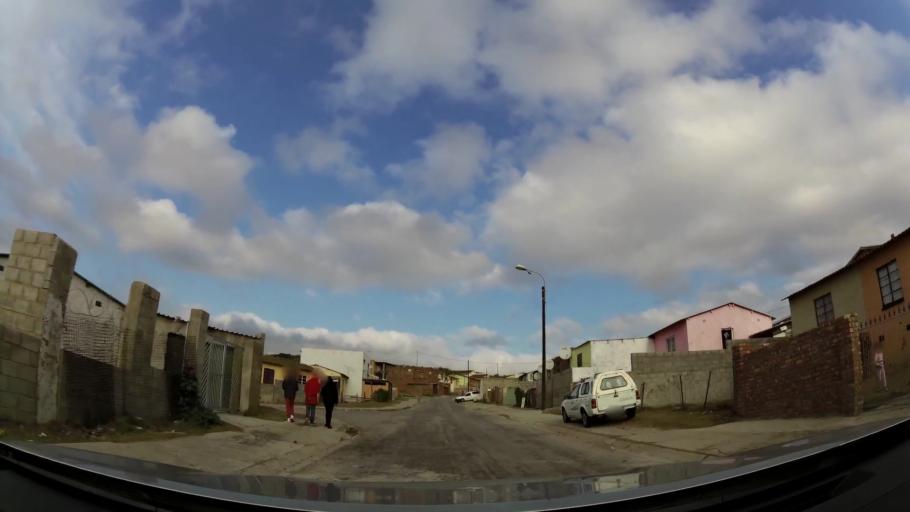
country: ZA
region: Eastern Cape
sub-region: Nelson Mandela Bay Metropolitan Municipality
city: Port Elizabeth
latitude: -33.9156
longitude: 25.5446
